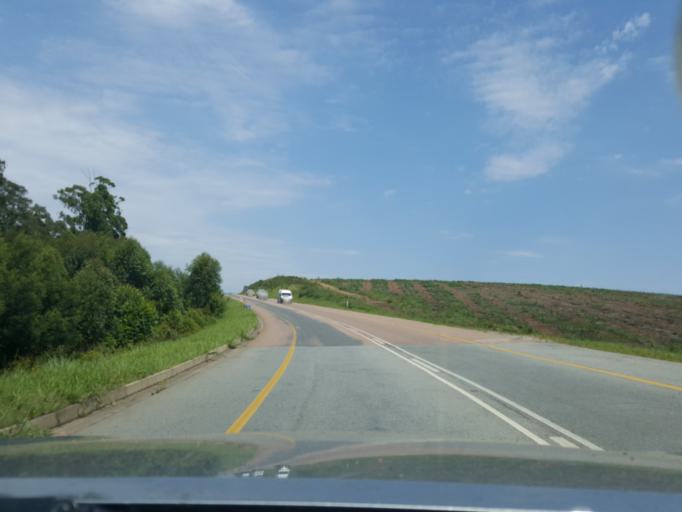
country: ZA
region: Mpumalanga
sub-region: Ehlanzeni District
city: White River
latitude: -25.1961
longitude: 31.0338
